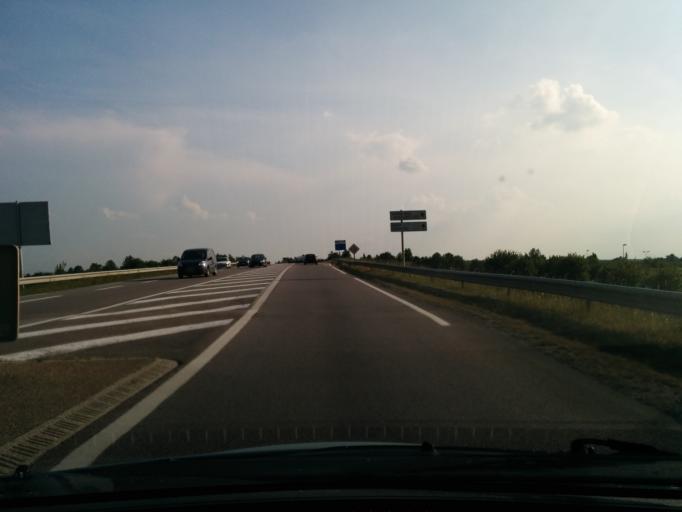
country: FR
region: Haute-Normandie
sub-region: Departement de l'Eure
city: Saint-Aubin-sur-Gaillon
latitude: 49.1382
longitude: 1.3155
